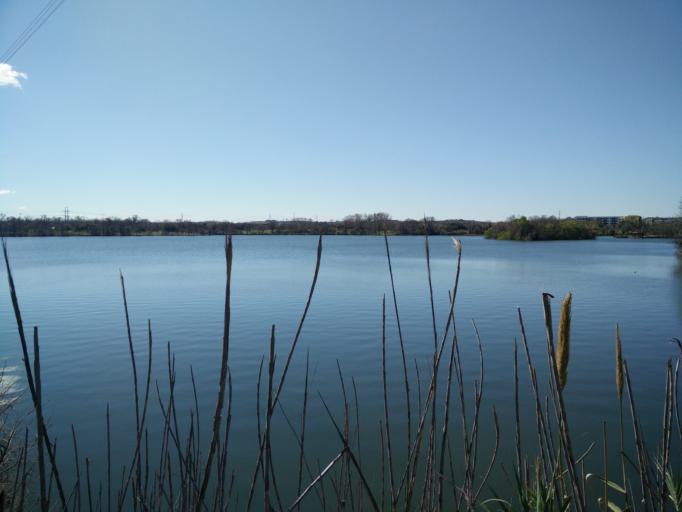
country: US
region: Texas
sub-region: Travis County
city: Austin
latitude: 30.2503
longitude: -97.7184
